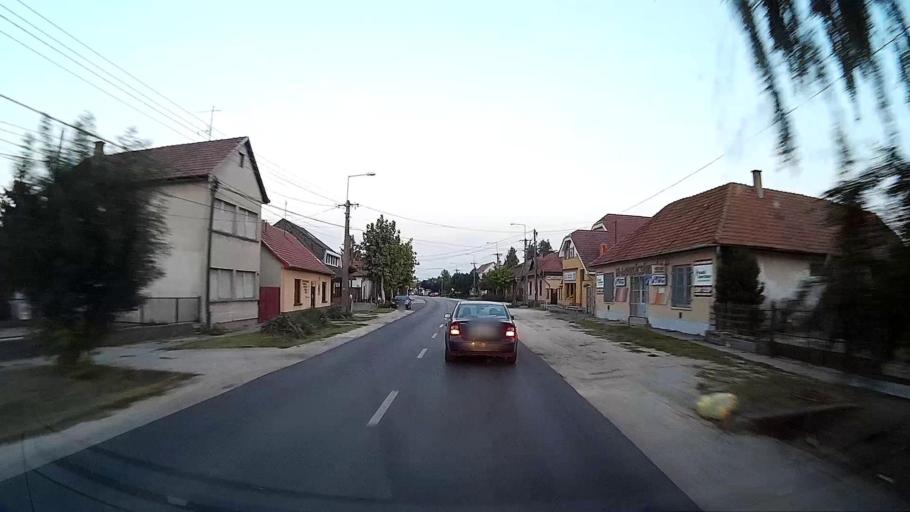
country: HU
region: Pest
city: Albertirsa
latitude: 47.2477
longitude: 19.6115
